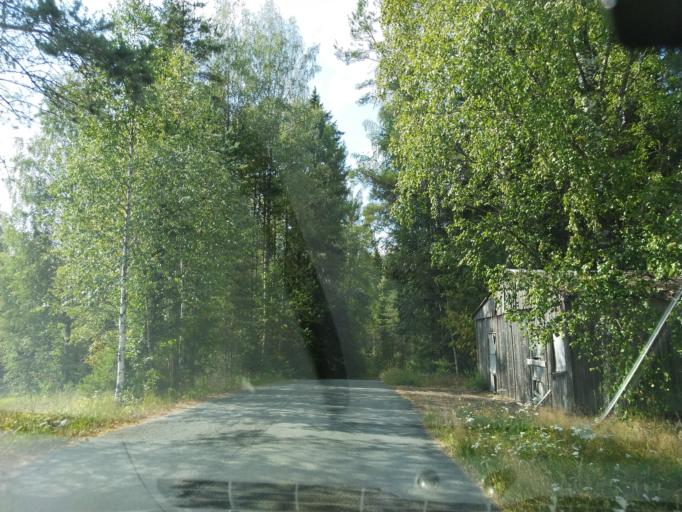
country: FI
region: Uusimaa
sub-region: Helsinki
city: Karkkila
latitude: 60.7189
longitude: 24.1826
